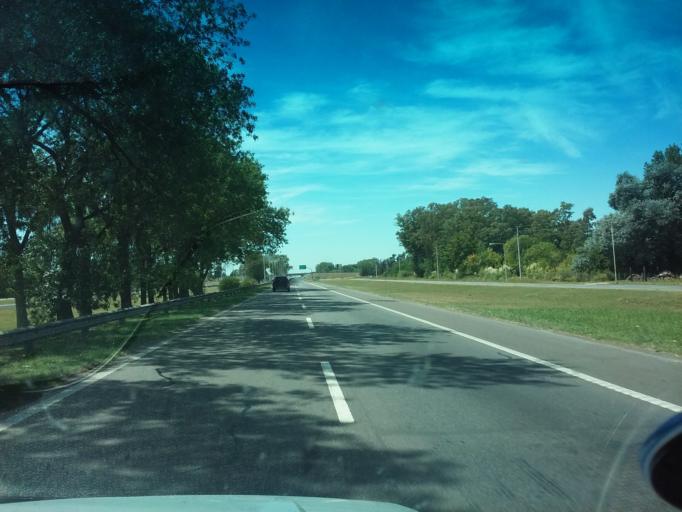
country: AR
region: Buenos Aires
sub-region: Partido de Mercedes
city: Mercedes
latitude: -34.6578
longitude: -59.3618
